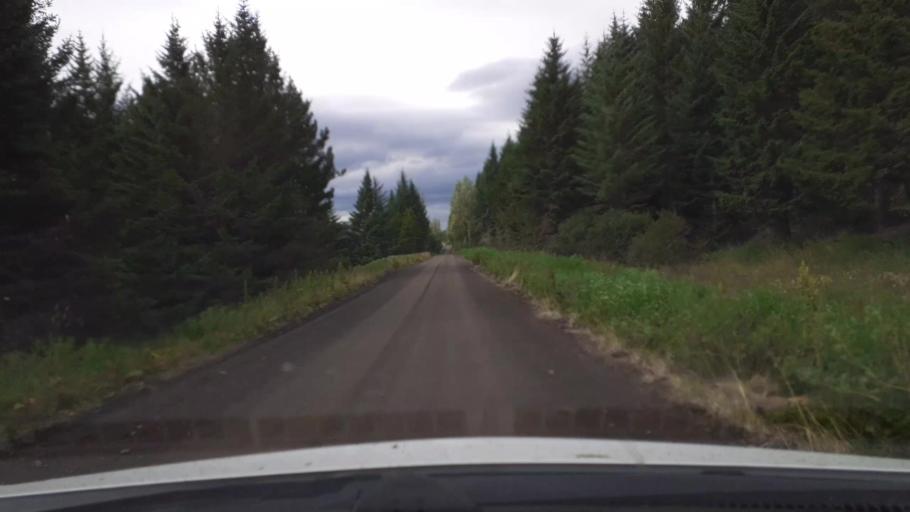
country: IS
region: Capital Region
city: Mosfellsbaer
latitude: 64.5209
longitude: -21.4497
